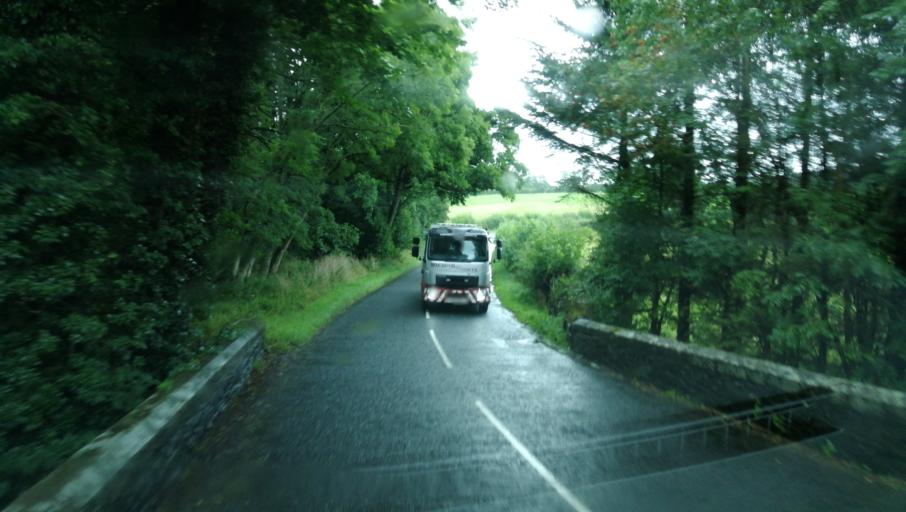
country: GB
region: England
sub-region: Cumbria
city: Penrith
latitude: 54.5964
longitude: -2.8600
